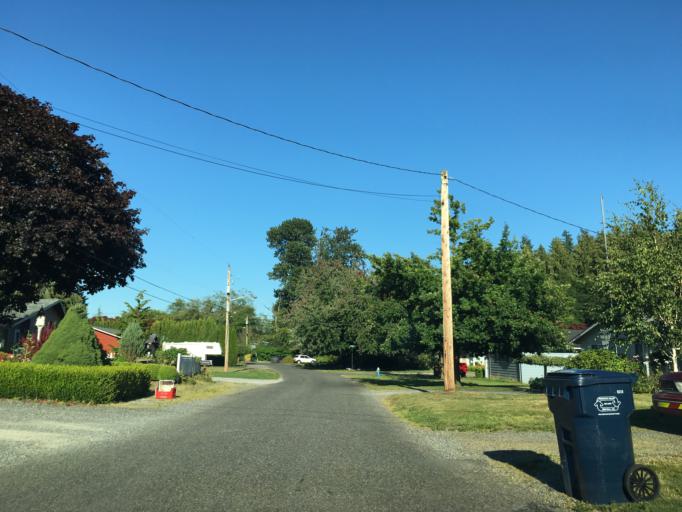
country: US
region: Washington
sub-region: Whatcom County
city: Lynden
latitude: 48.9507
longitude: -122.4518
